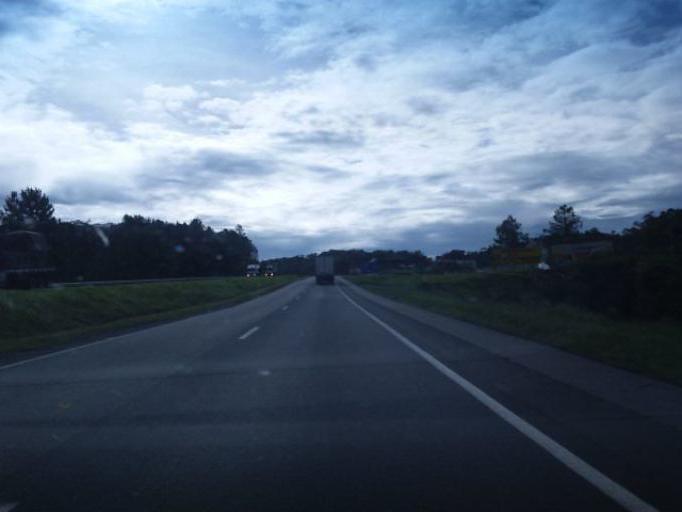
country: BR
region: Parana
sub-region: Antonina
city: Antonina
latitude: -25.1033
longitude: -48.7026
